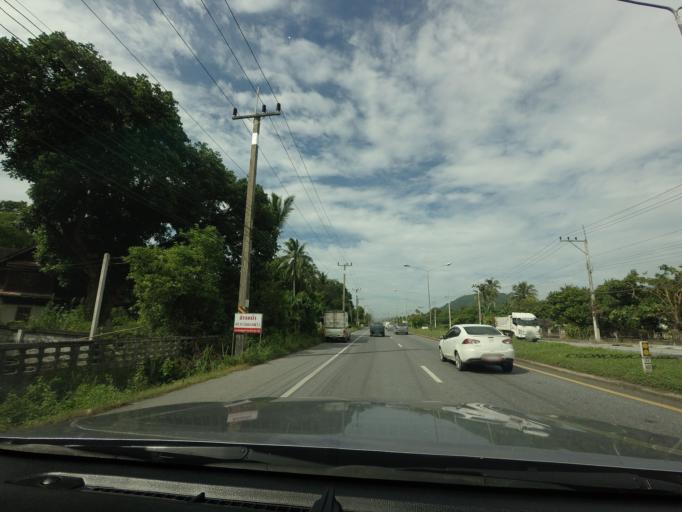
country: TH
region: Nakhon Si Thammarat
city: Ron Phibun
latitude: 8.2174
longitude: 99.8692
